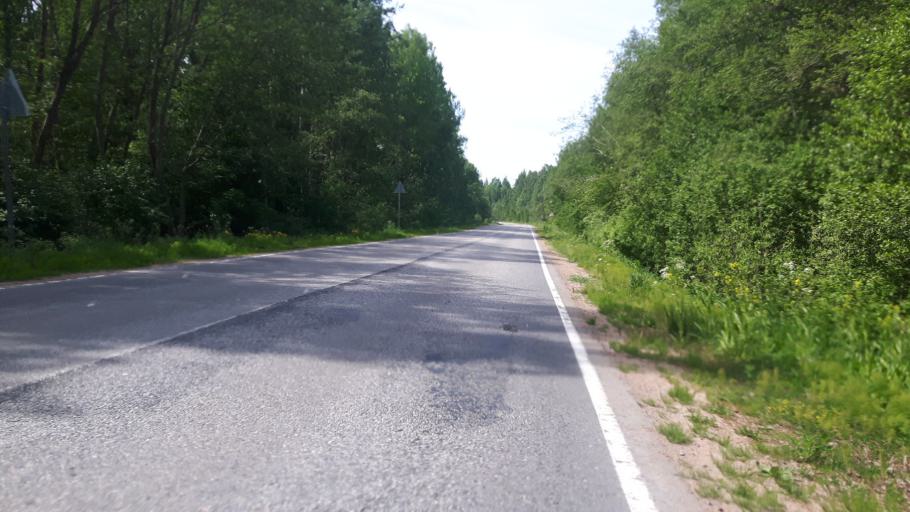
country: RU
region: Leningrad
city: Ust'-Luga
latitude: 59.6467
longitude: 28.2074
